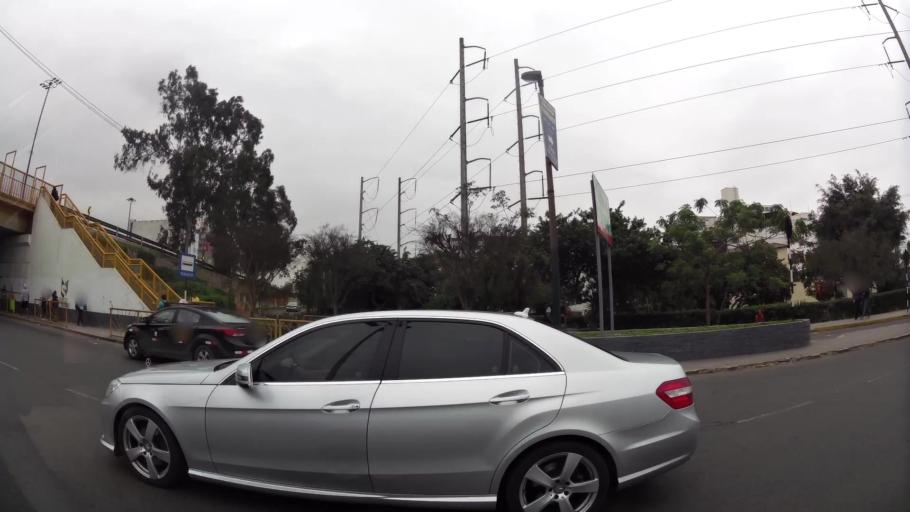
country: PE
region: Lima
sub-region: Lima
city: San Luis
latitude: -12.1103
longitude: -76.9787
